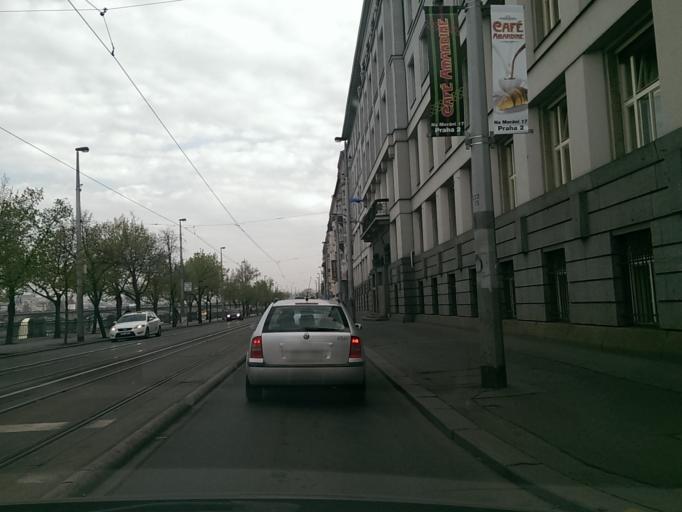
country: CZ
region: Praha
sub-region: Praha 2
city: Vysehrad
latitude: 50.0692
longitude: 14.4148
